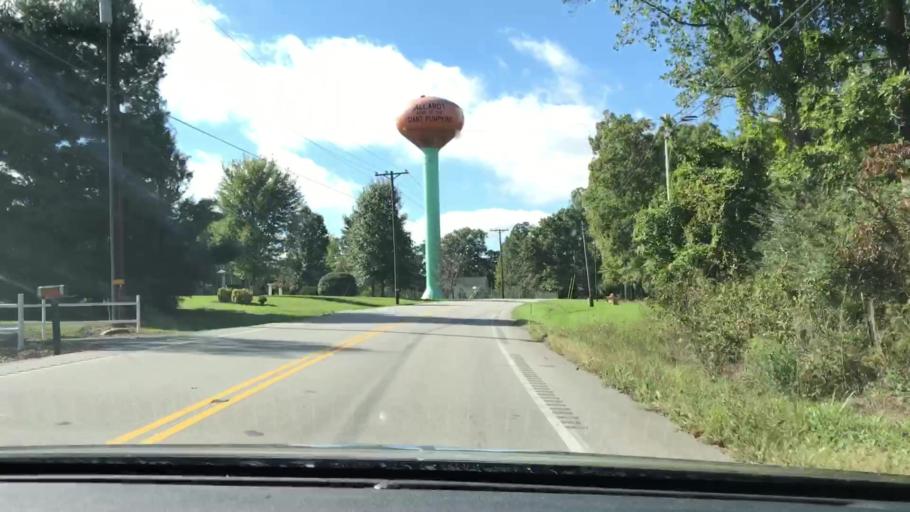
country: US
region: Tennessee
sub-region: Fentress County
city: Jamestown
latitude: 36.3739
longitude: -84.8700
